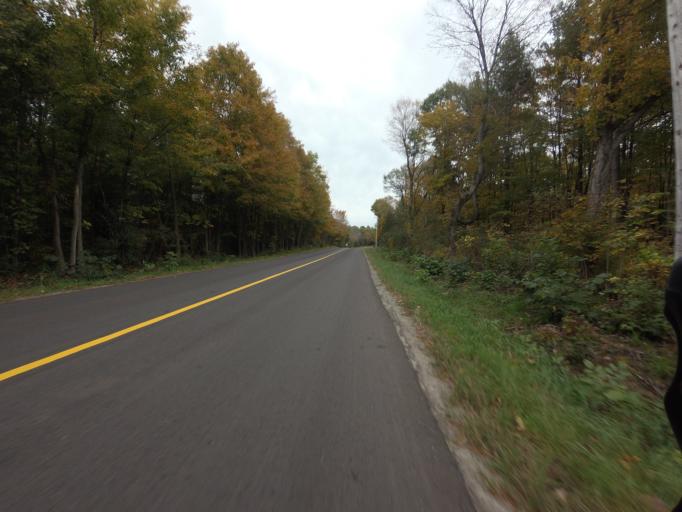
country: CA
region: Ontario
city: Gananoque
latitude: 44.5795
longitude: -76.0807
